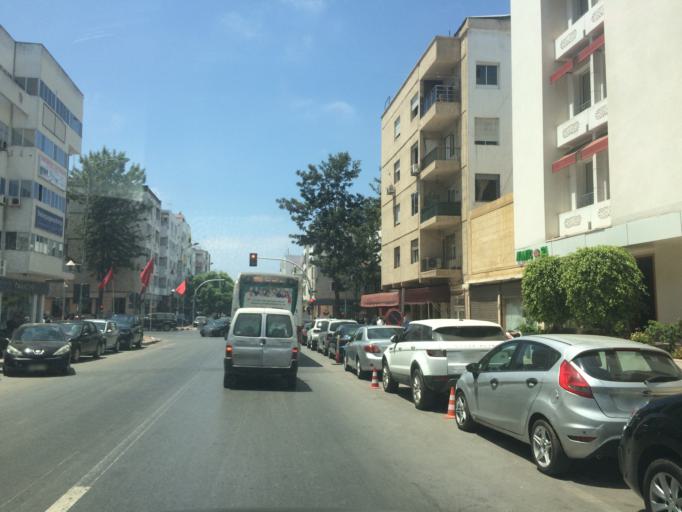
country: MA
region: Rabat-Sale-Zemmour-Zaer
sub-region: Rabat
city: Rabat
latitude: 33.9964
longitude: -6.8474
